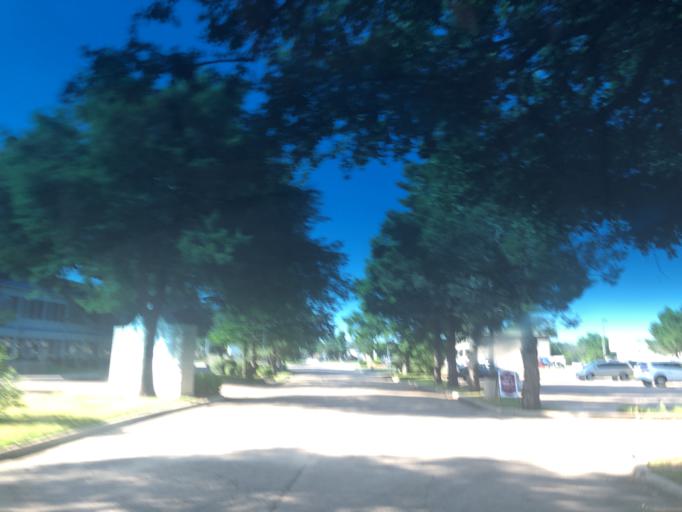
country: US
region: Texas
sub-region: Dallas County
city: Grand Prairie
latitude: 32.7112
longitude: -97.0037
